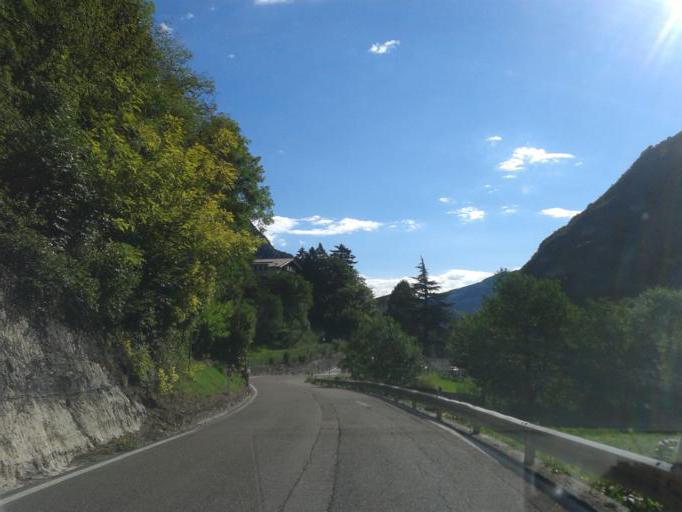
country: IT
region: Trentino-Alto Adige
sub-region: Provincia di Trento
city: Molina di Ledro
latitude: 45.8656
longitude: 10.8010
